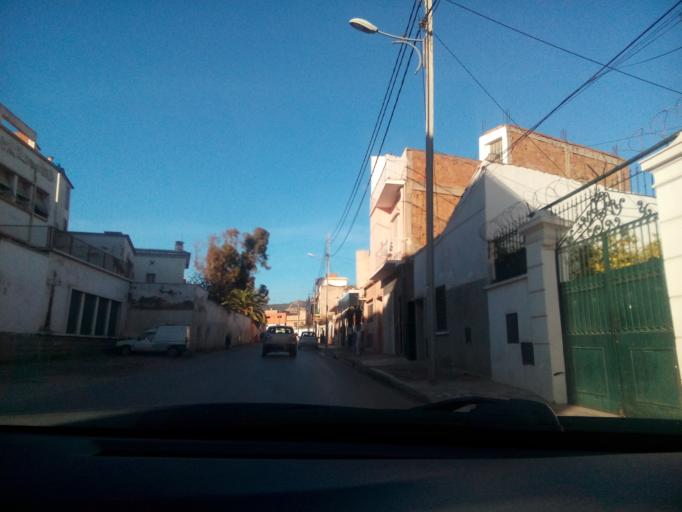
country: DZ
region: Oran
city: Oran
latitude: 35.6877
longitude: -0.6631
